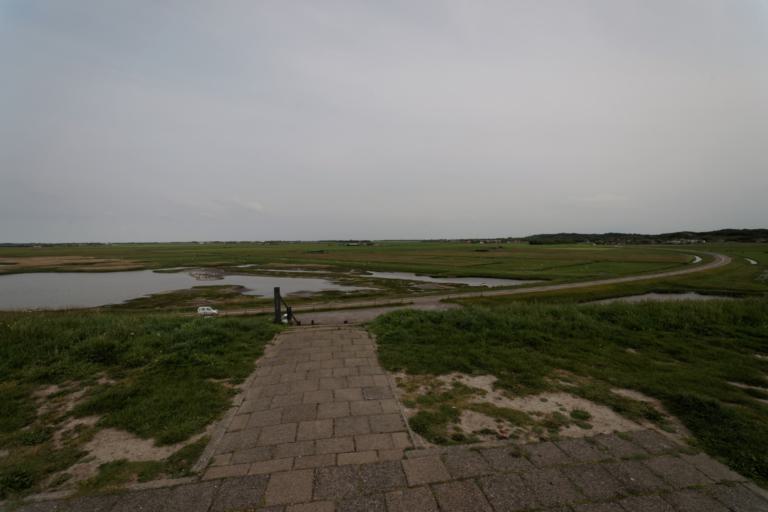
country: NL
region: North Holland
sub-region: Gemeente Bergen
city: Egmond aan Zee
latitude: 52.7339
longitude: 4.6421
